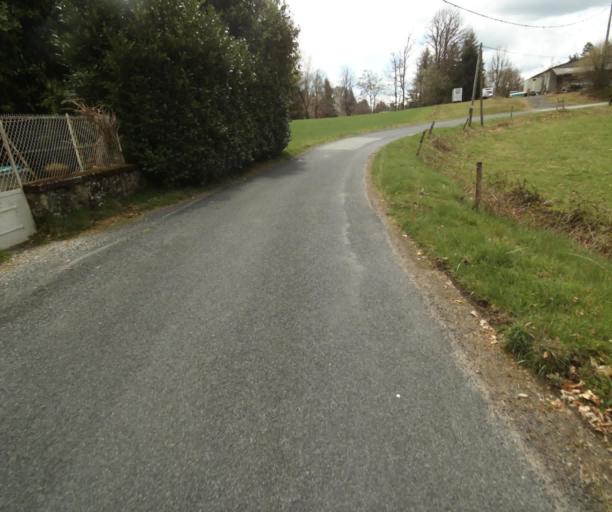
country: FR
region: Limousin
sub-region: Departement de la Correze
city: Correze
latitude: 45.3553
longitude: 1.9318
